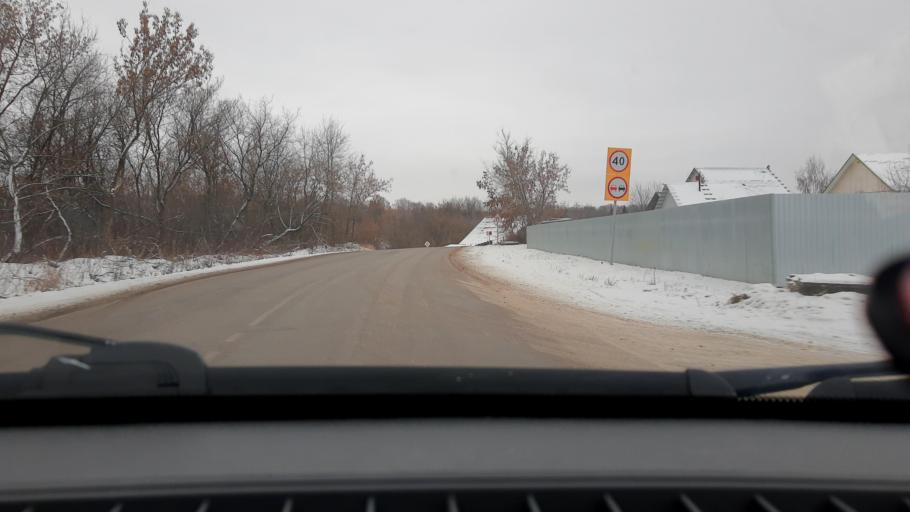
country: RU
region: Bashkortostan
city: Iglino
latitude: 54.8411
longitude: 56.4511
